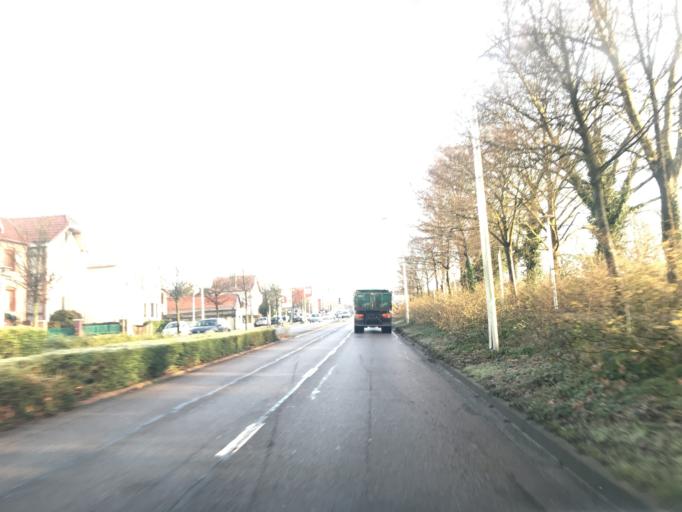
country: FR
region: Haute-Normandie
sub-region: Departement de la Seine-Maritime
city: Le Petit-Quevilly
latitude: 49.4083
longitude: 1.0701
